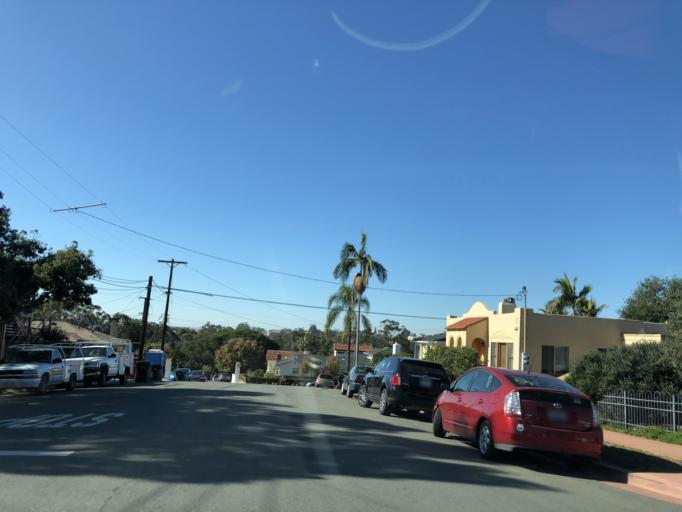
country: US
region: California
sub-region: San Diego County
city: San Diego
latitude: 32.7286
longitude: -117.1311
